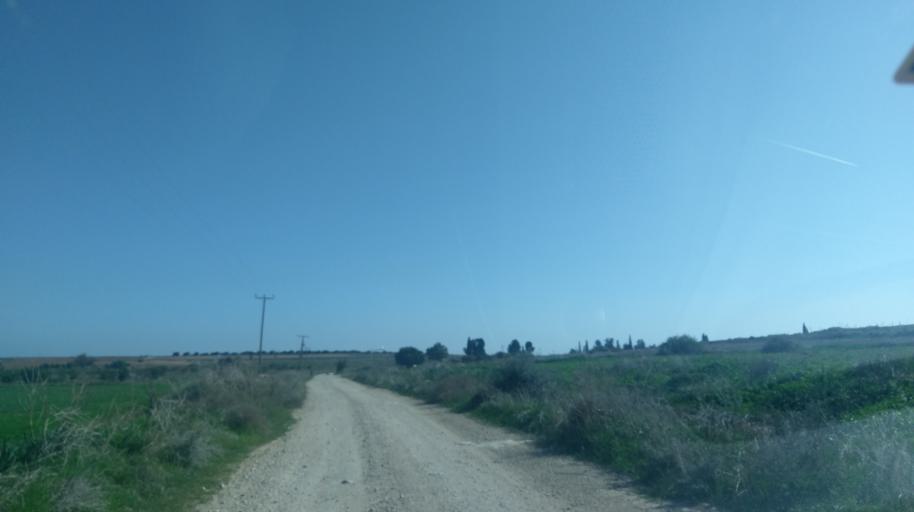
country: CY
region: Ammochostos
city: Trikomo
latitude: 35.2558
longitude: 33.8386
